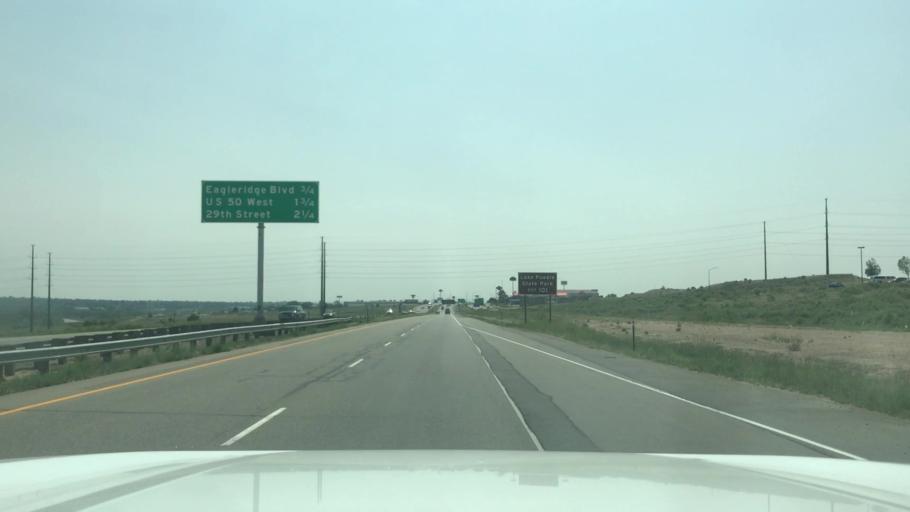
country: US
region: Colorado
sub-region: Pueblo County
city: Pueblo
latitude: 38.3334
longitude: -104.6185
